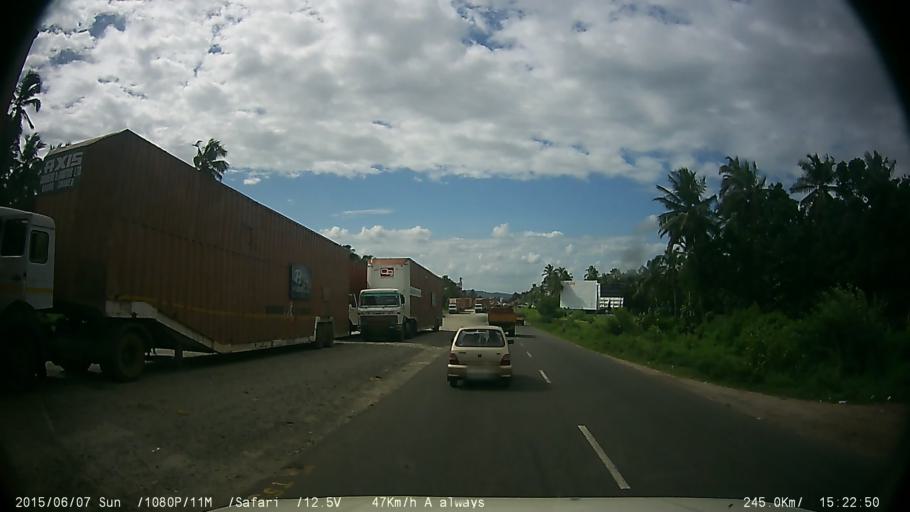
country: IN
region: Kerala
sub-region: Thrissur District
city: Trichur
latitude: 10.5183
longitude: 76.2587
